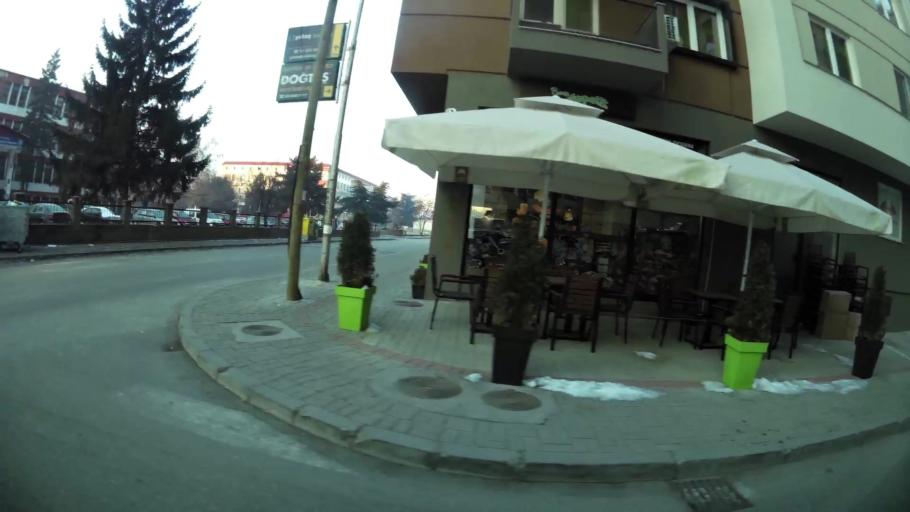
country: MK
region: Karpos
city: Skopje
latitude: 42.0054
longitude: 21.4103
